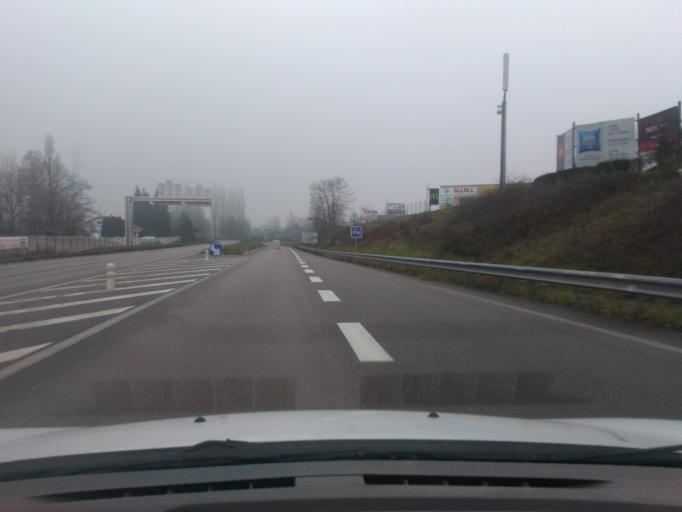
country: FR
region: Lorraine
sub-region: Departement des Vosges
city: Chavelot
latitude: 48.2237
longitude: 6.4324
